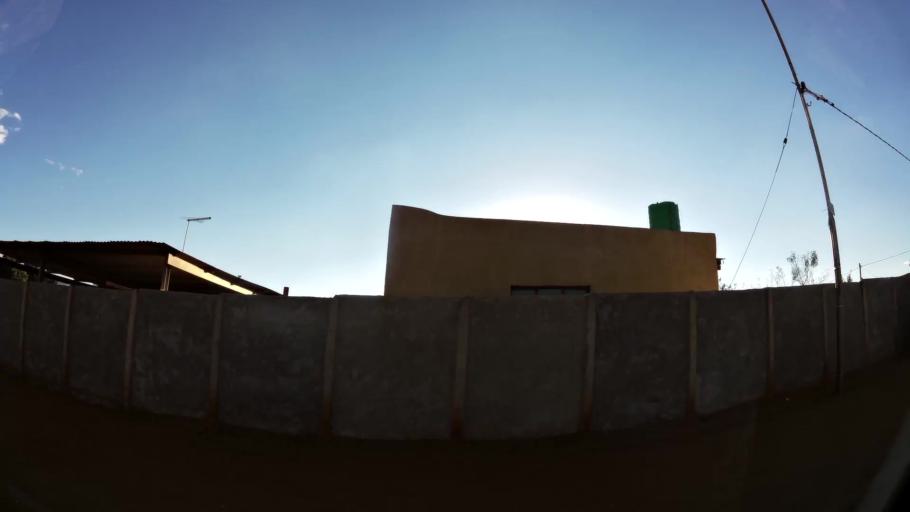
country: ZA
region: Limpopo
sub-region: Waterberg District Municipality
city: Mokopane
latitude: -24.1512
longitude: 28.9866
